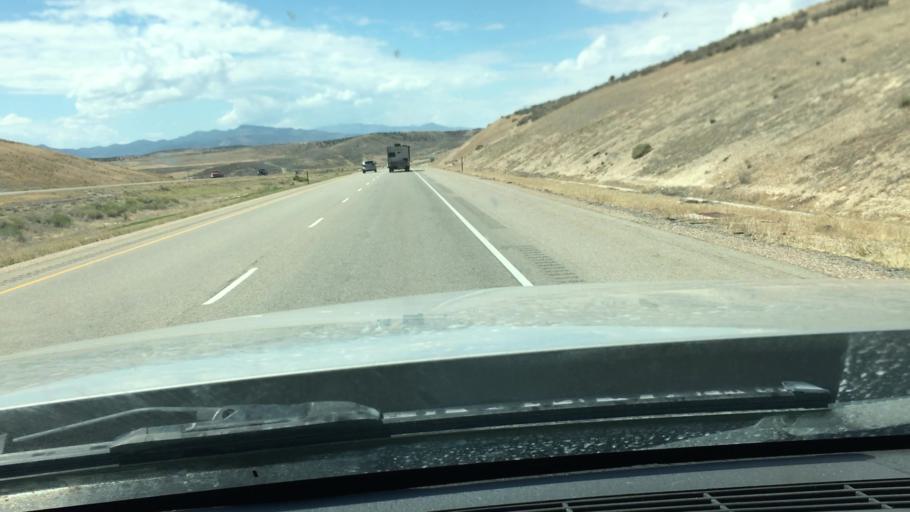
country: US
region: Utah
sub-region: Juab County
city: Nephi
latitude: 39.4987
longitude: -111.9668
